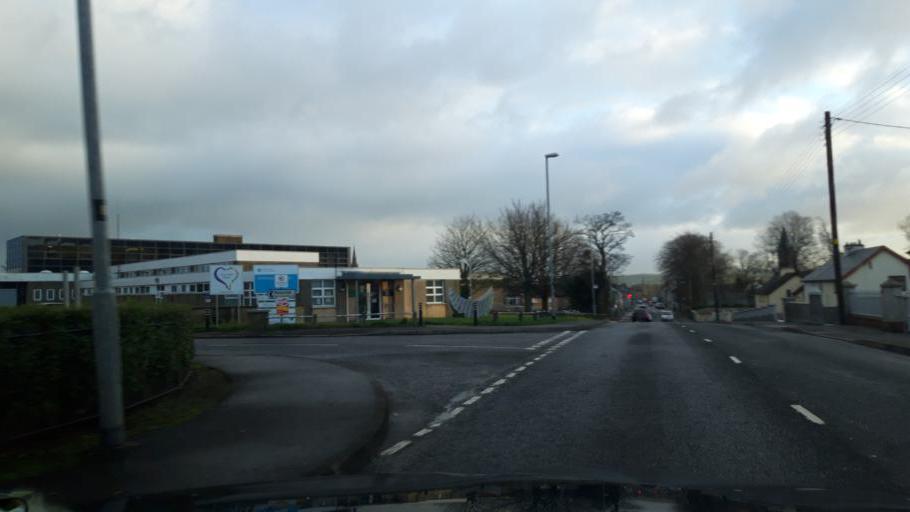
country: GB
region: Northern Ireland
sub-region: Moyle District
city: Ballycastle
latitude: 55.1997
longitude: -6.2587
